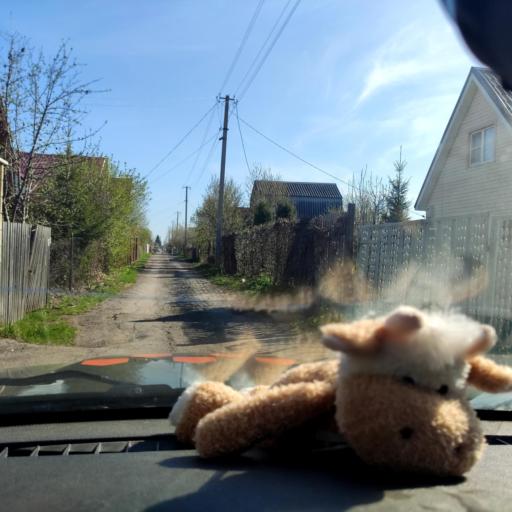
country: RU
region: Samara
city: Tol'yatti
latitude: 53.6001
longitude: 49.2654
